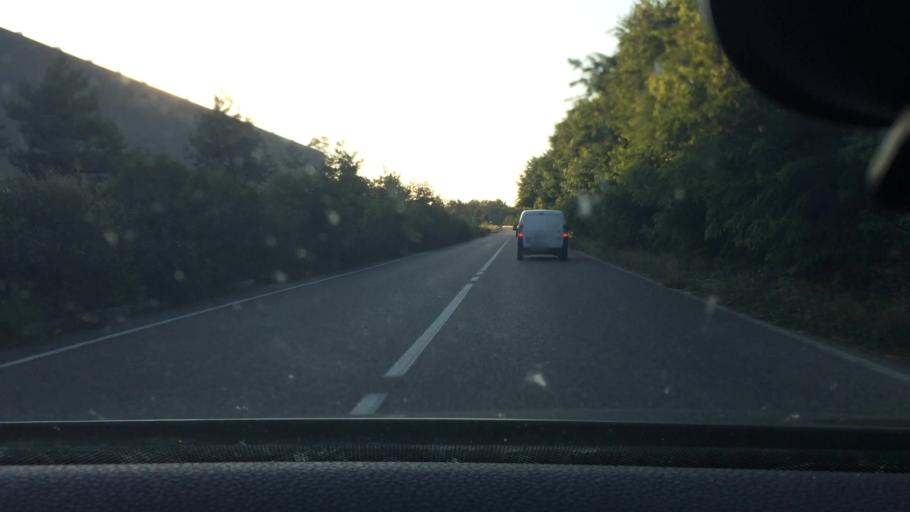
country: IT
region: Lombardy
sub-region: Citta metropolitana di Milano
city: Rescaldina
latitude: 45.6192
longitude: 8.9642
